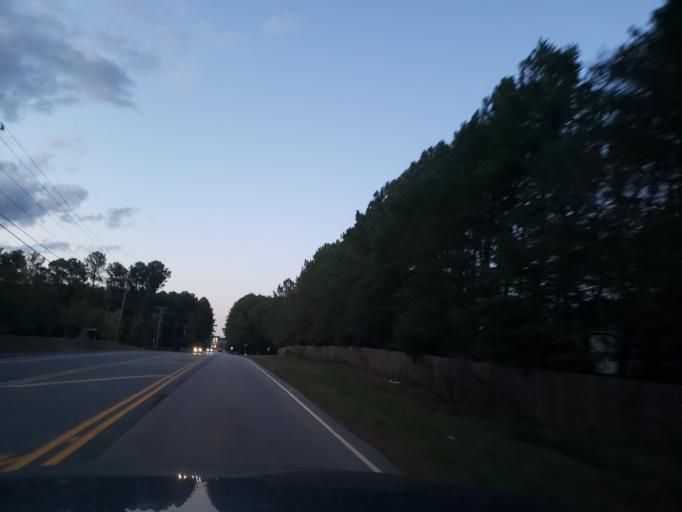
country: US
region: North Carolina
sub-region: Orange County
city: Chapel Hill
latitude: 35.8922
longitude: -78.9580
